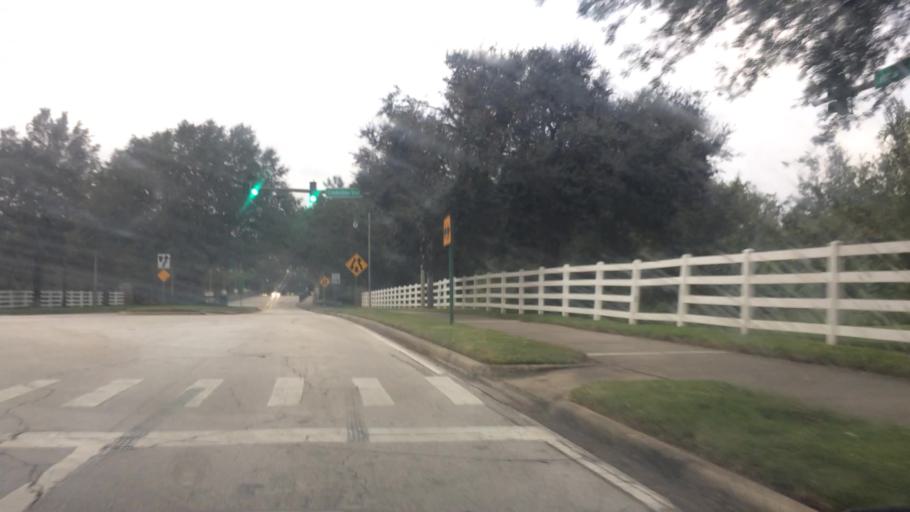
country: US
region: Florida
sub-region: Osceola County
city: Celebration
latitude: 28.3247
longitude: -81.5327
